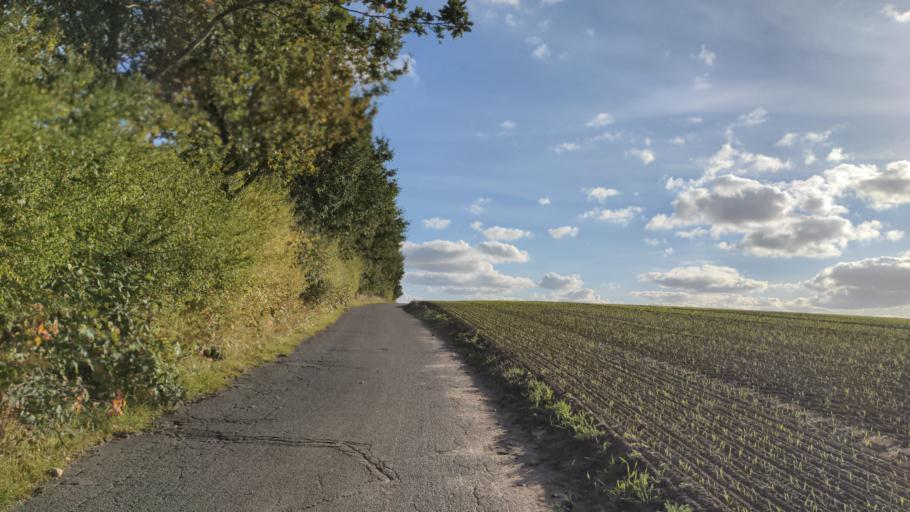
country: DE
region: Schleswig-Holstein
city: Schashagen
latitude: 54.1424
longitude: 10.9033
